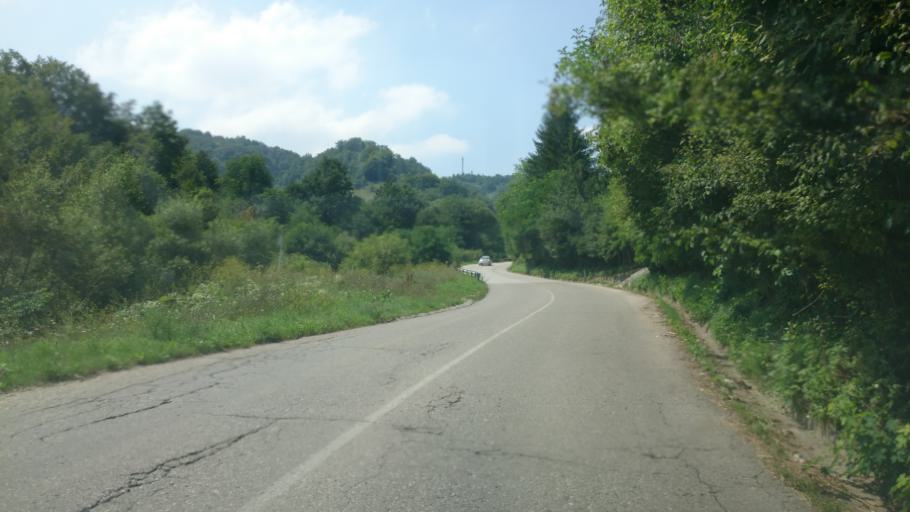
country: BA
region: Federation of Bosnia and Herzegovina
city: Lokvine
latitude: 44.1893
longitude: 17.8660
